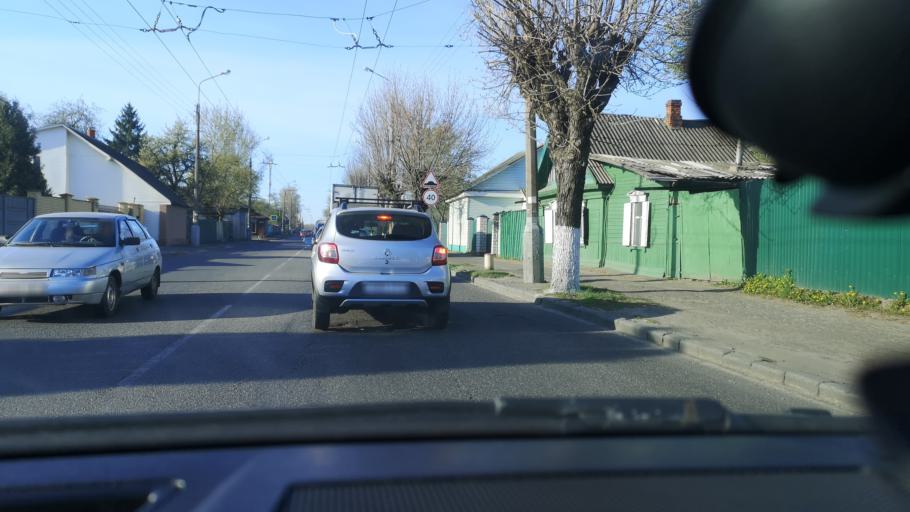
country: BY
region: Gomel
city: Gomel
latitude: 52.4364
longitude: 30.9769
